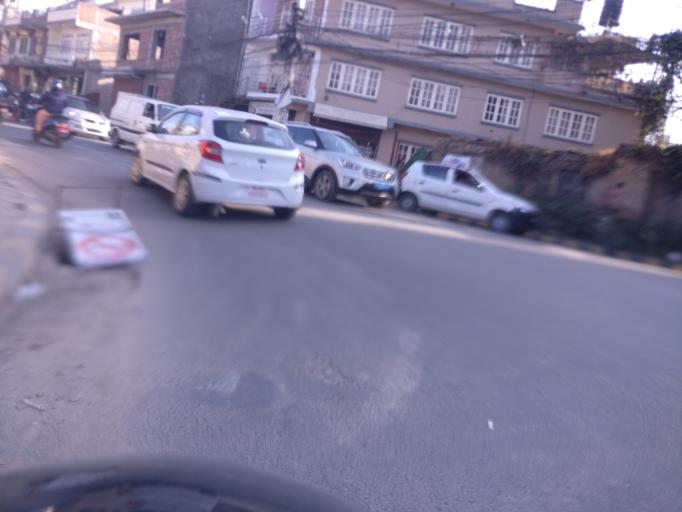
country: NP
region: Central Region
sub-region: Bagmati Zone
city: Patan
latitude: 27.6804
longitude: 85.3054
